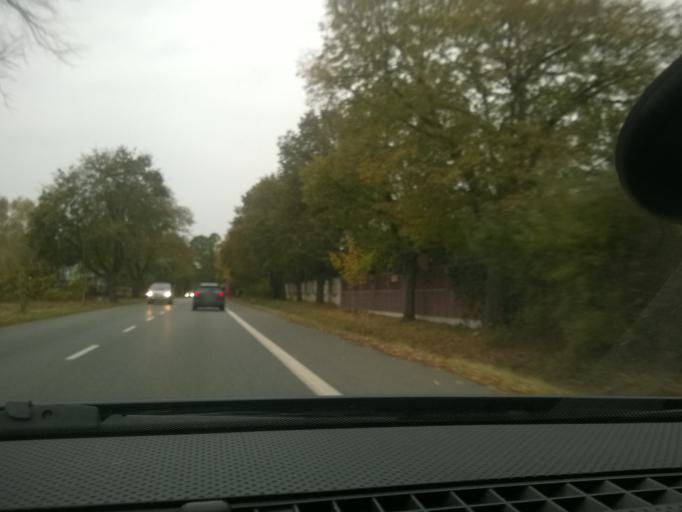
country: PL
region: Masovian Voivodeship
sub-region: Powiat pruszkowski
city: Komorow
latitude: 52.1579
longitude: 20.8256
